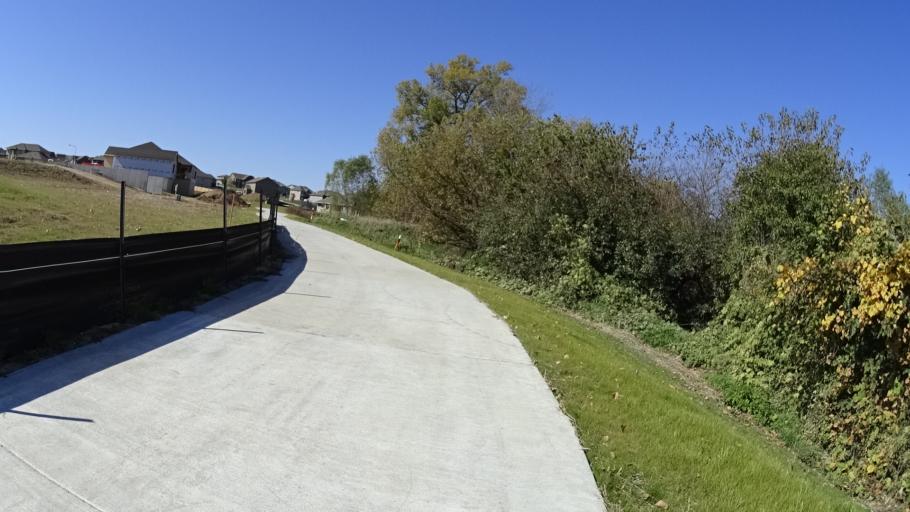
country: US
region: Nebraska
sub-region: Sarpy County
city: La Vista
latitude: 41.1663
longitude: -96.0144
